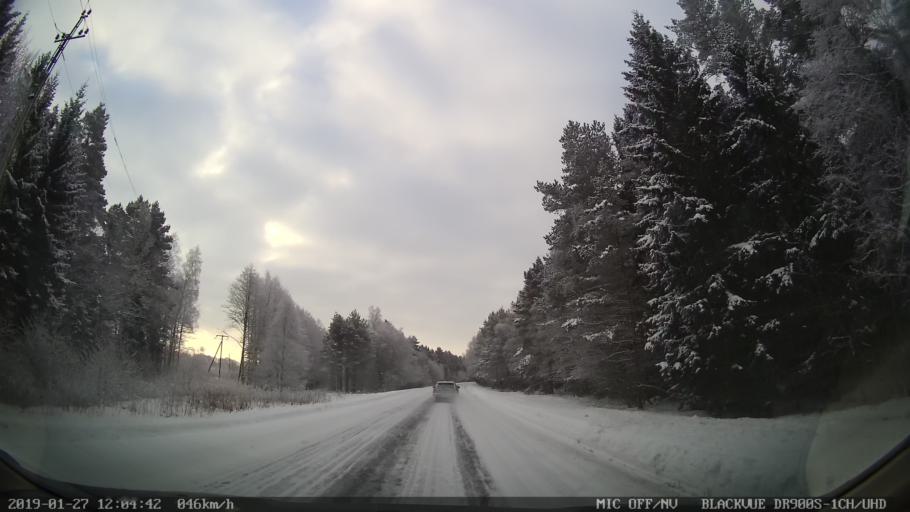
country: EE
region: Harju
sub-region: Raasiku vald
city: Raasiku
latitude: 59.4811
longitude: 25.2575
